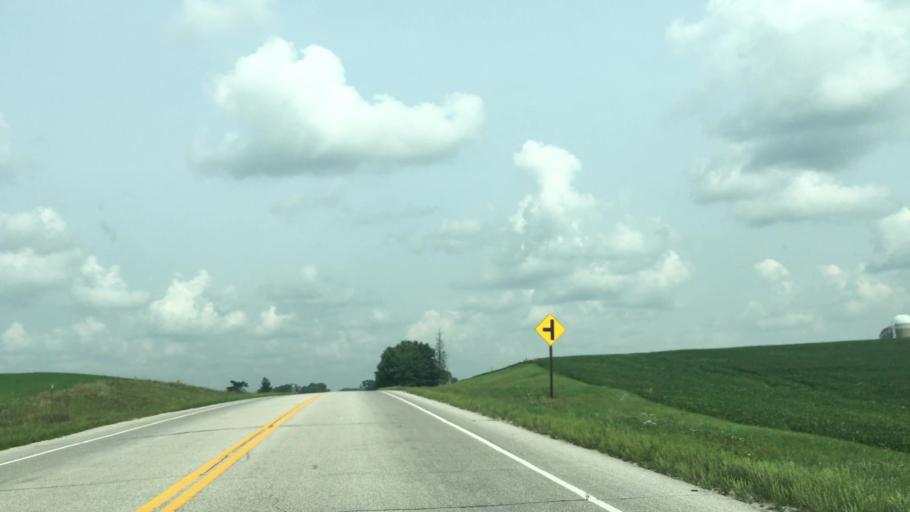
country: US
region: Minnesota
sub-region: Fillmore County
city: Harmony
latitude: 43.5996
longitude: -91.9297
